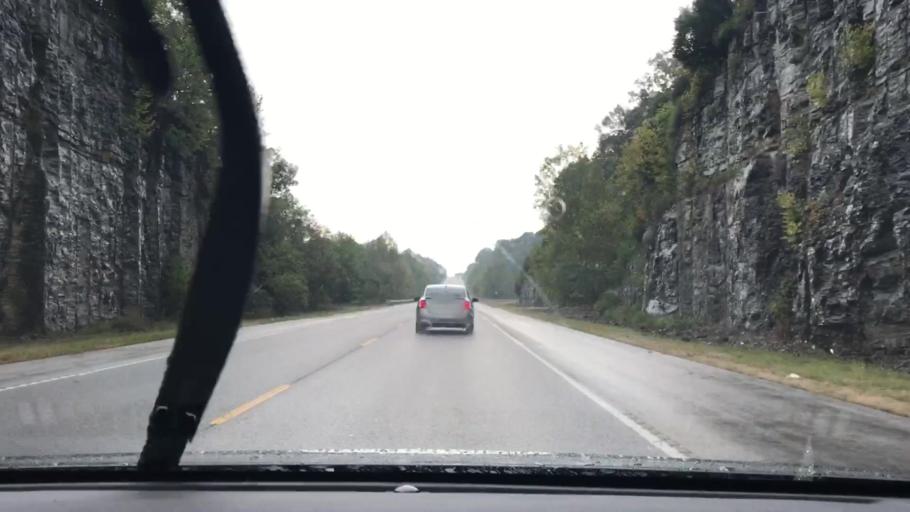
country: US
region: Tennessee
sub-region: Macon County
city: Red Boiling Springs
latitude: 36.5067
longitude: -85.9307
